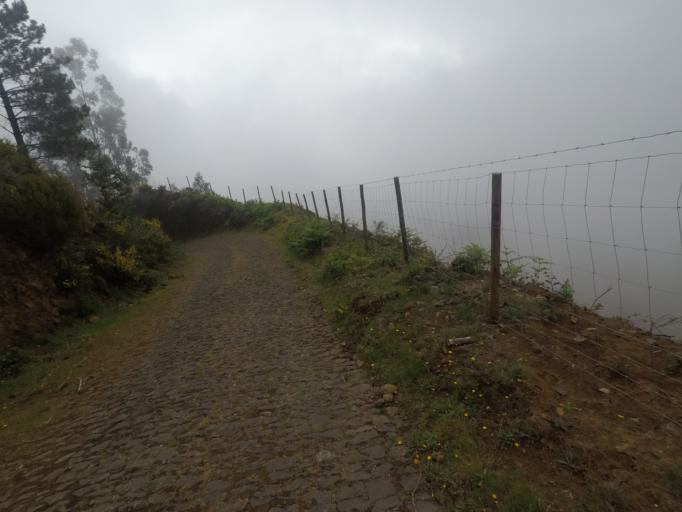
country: PT
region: Madeira
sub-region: Calheta
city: Arco da Calheta
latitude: 32.7305
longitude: -17.0971
